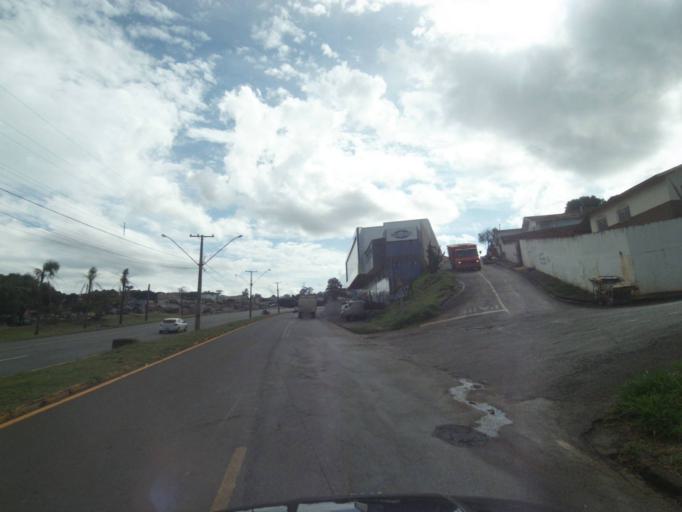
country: BR
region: Parana
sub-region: Telemaco Borba
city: Telemaco Borba
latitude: -24.3297
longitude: -50.6377
